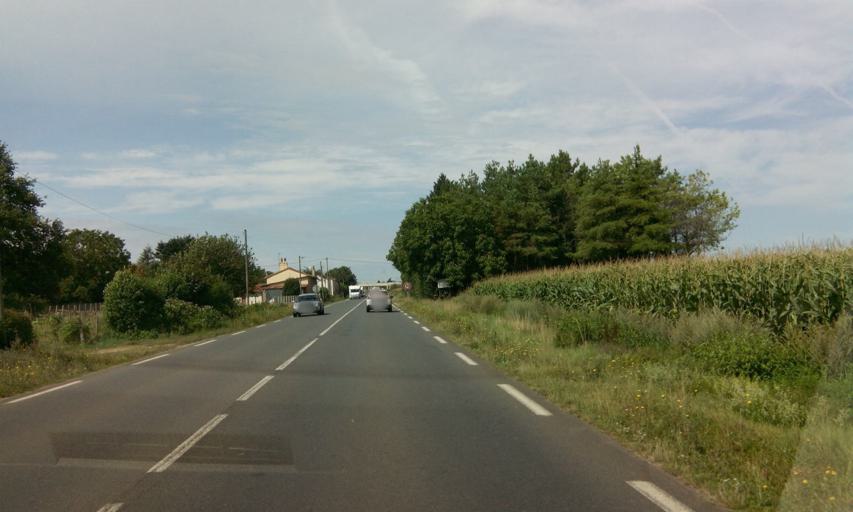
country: FR
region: Poitou-Charentes
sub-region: Departement des Deux-Sevres
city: Sauze-Vaussais
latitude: 46.1355
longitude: 0.1415
